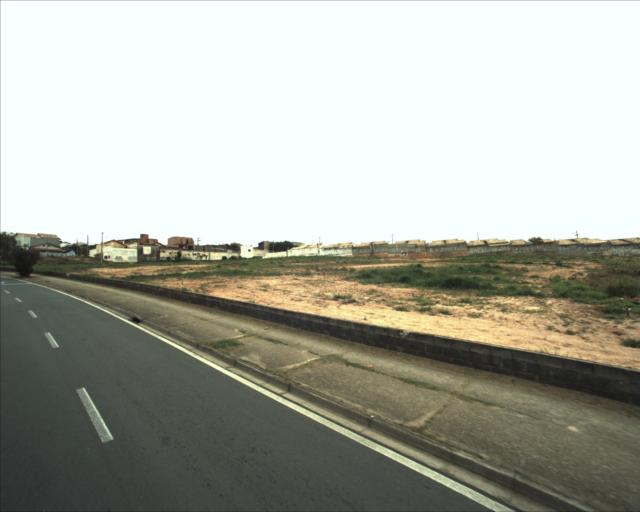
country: BR
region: Sao Paulo
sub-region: Sorocaba
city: Sorocaba
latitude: -23.4891
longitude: -47.4989
